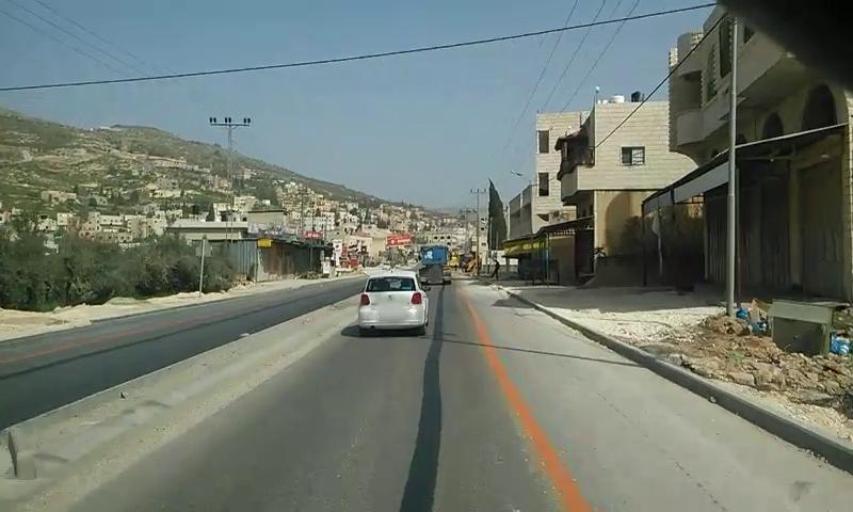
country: PS
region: West Bank
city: Huwwarah
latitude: 32.1452
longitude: 35.2580
